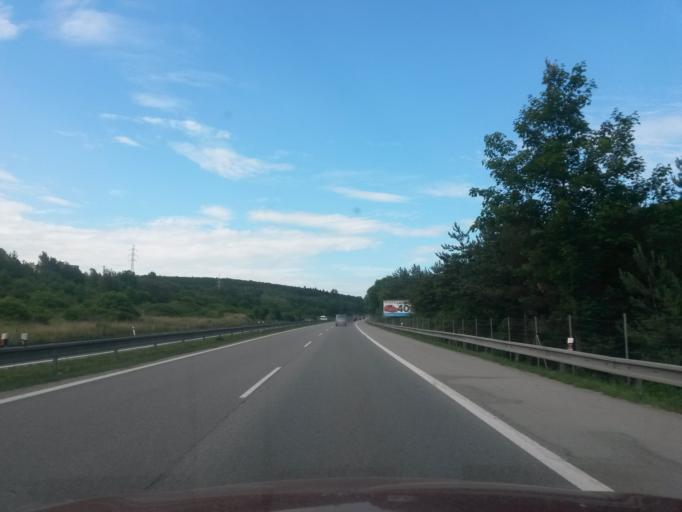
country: SK
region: Kosicky
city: Kosice
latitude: 48.7511
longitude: 21.2759
